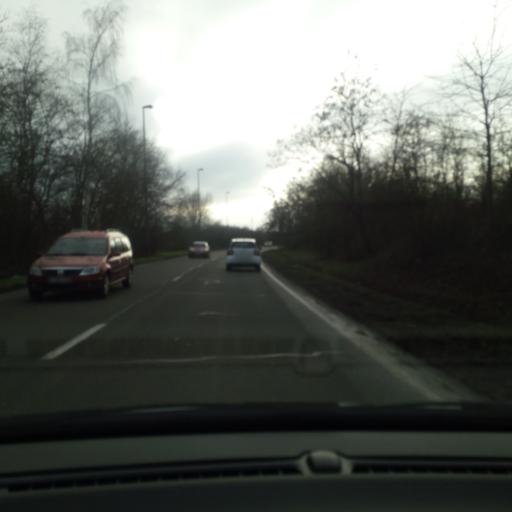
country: BE
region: Wallonia
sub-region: Province du Hainaut
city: Colfontaine
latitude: 50.4216
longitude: 3.8289
